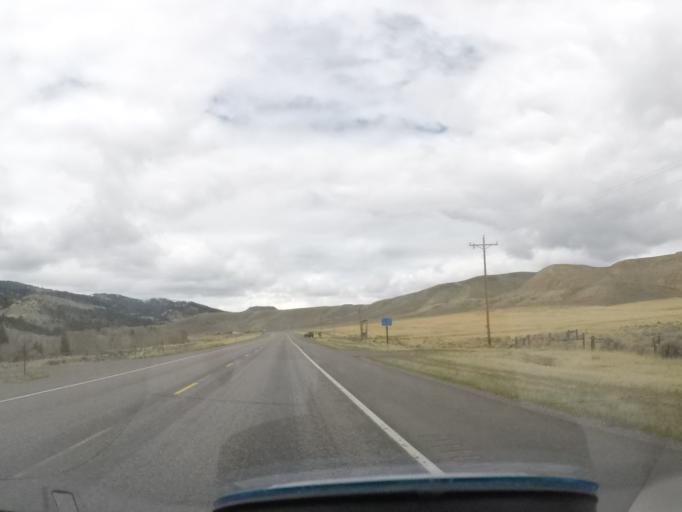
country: US
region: Wyoming
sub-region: Sublette County
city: Pinedale
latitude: 43.5768
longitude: -109.7373
